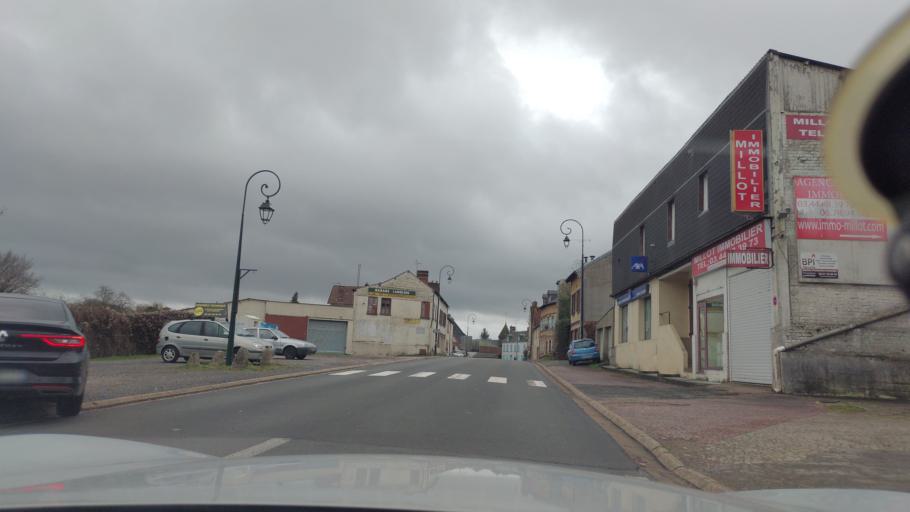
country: FR
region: Picardie
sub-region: Departement de l'Oise
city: Saint-Omer-en-Chaussee
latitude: 49.5787
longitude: 1.9538
